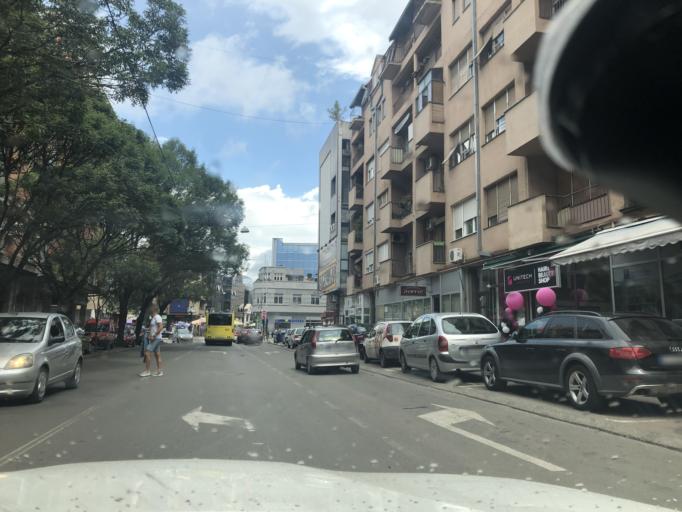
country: RS
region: Central Serbia
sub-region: Nisavski Okrug
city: Nis
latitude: 43.3161
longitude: 21.8946
